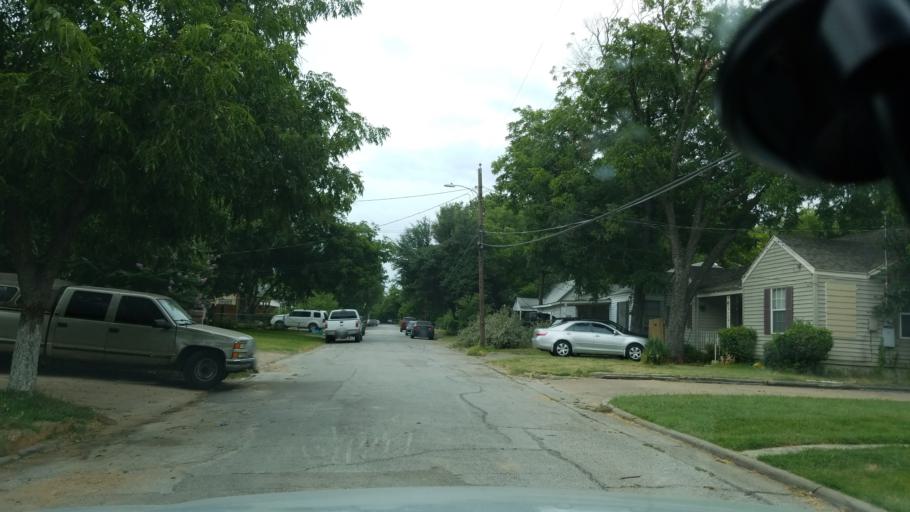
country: US
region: Texas
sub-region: Dallas County
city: Grand Prairie
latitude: 32.7431
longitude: -96.9955
